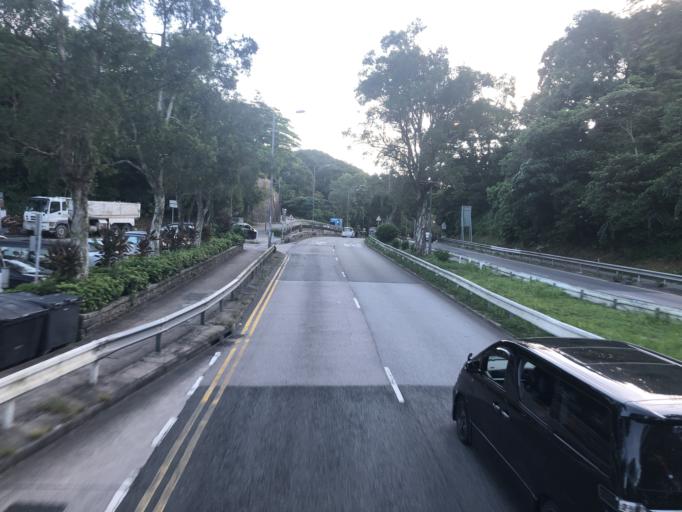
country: HK
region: Wong Tai Sin
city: Wong Tai Sin
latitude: 22.3337
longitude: 114.2369
